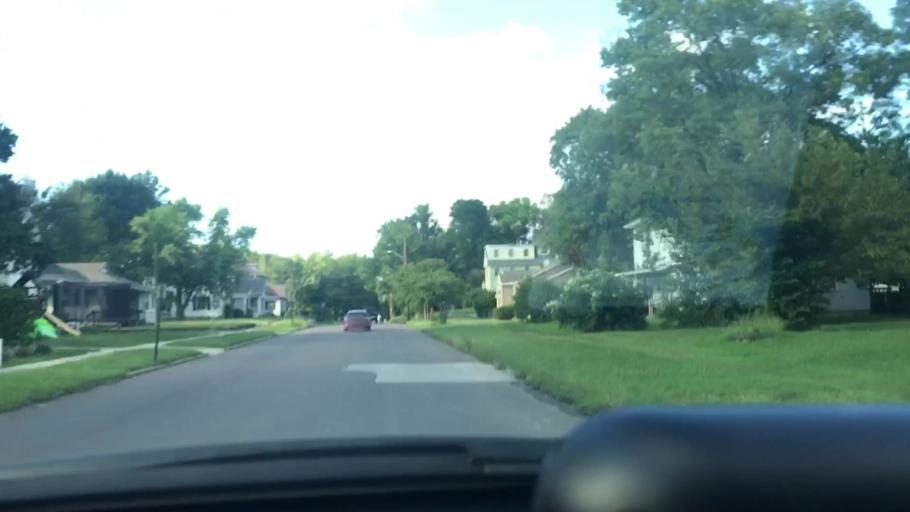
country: US
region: Missouri
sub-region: Pettis County
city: Sedalia
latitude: 38.7019
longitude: -93.2366
